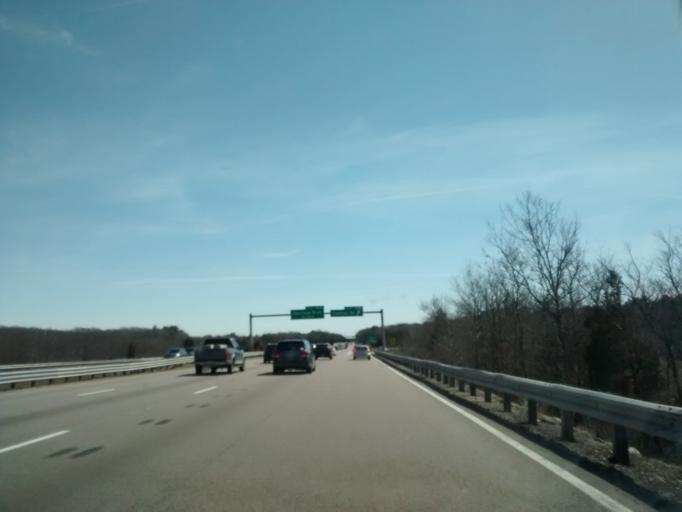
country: US
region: Massachusetts
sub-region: Norfolk County
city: Avon
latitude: 42.1295
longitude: -71.0633
